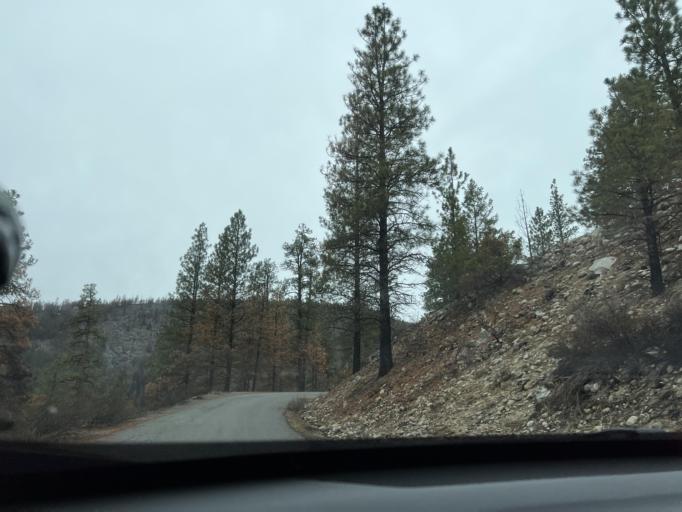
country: US
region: Washington
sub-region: Okanogan County
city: Brewster
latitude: 48.5801
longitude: -120.1666
